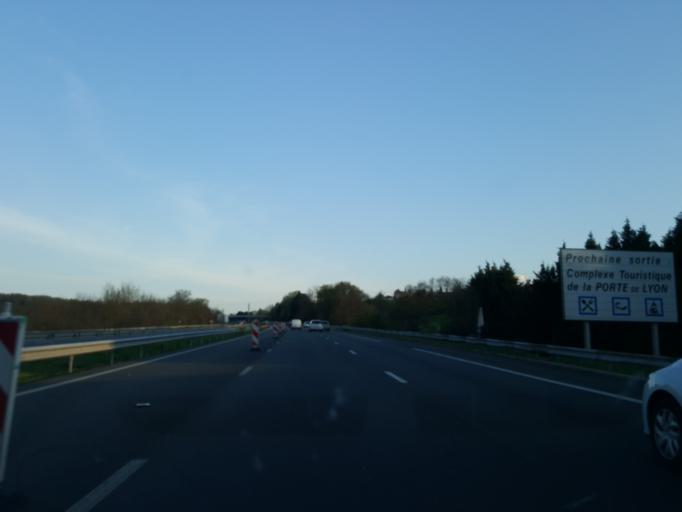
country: FR
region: Rhone-Alpes
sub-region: Departement du Rhone
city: Lissieu
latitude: 45.8497
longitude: 4.7452
